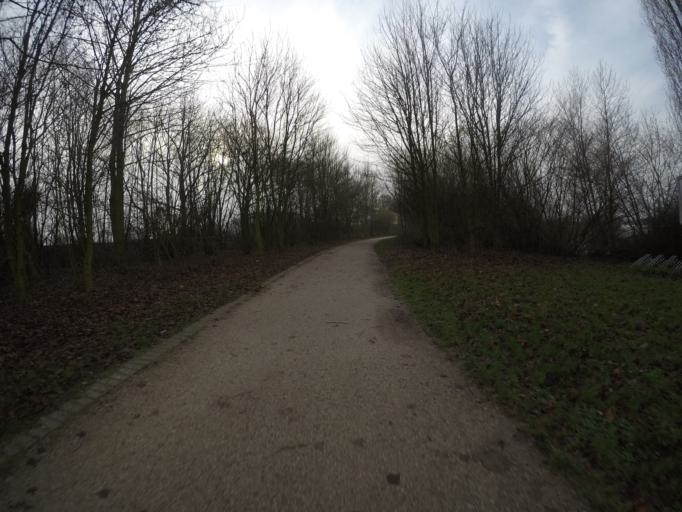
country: DE
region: North Rhine-Westphalia
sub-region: Regierungsbezirk Dusseldorf
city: Xanten
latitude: 51.6787
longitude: 6.4565
